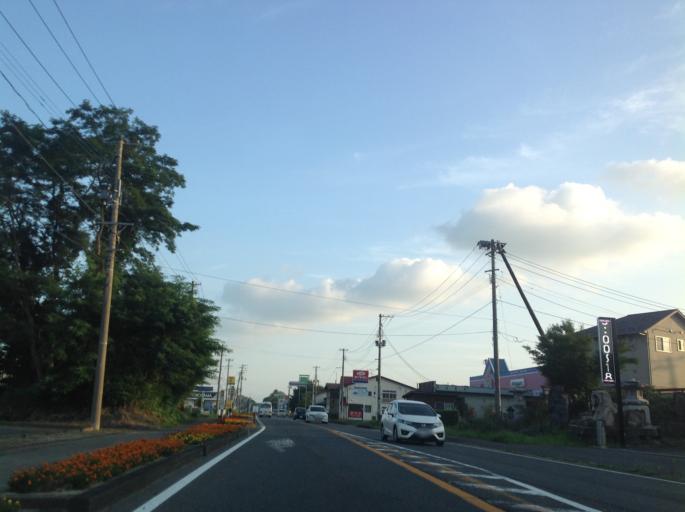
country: JP
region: Iwate
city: Hanamaki
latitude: 39.3592
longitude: 141.1128
